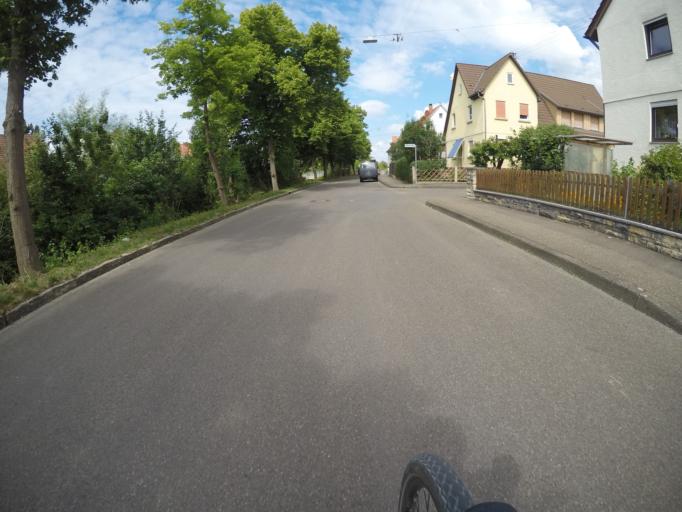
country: DE
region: Baden-Wuerttemberg
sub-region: Regierungsbezirk Stuttgart
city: Wendlingen am Neckar
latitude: 48.6717
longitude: 9.3905
